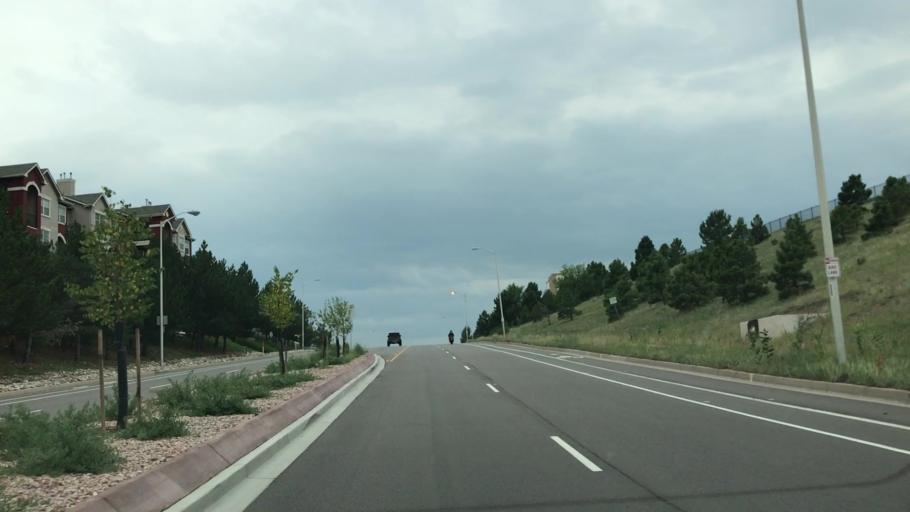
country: US
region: Colorado
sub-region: El Paso County
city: Colorado Springs
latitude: 38.8837
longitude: -104.8477
